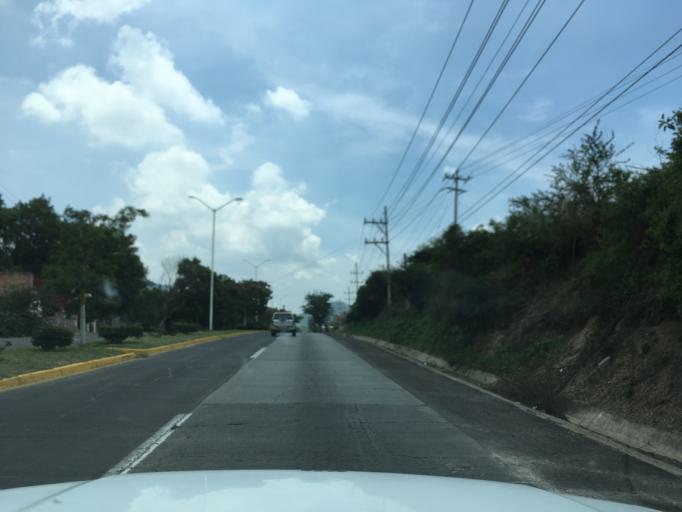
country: MX
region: Jalisco
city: Tlajomulco de Zuniga
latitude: 20.4893
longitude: -103.4639
